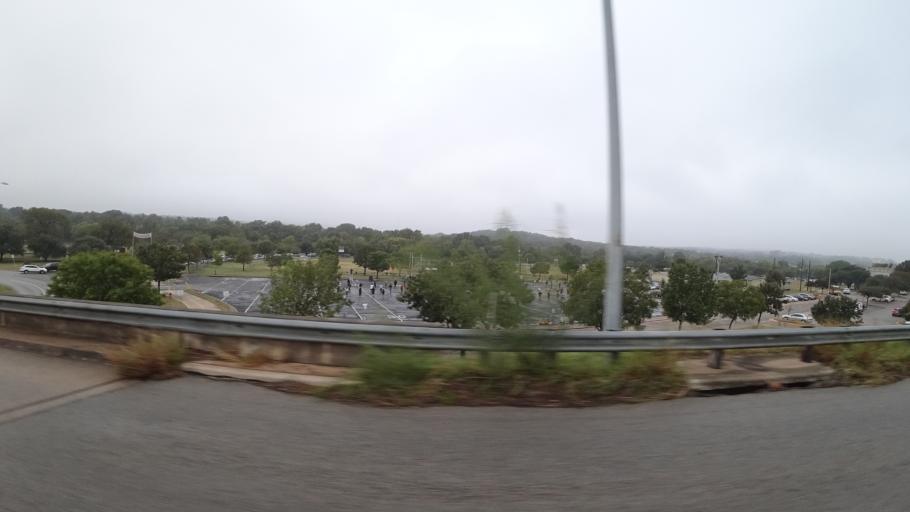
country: US
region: Texas
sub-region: Travis County
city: Austin
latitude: 30.2725
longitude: -97.7647
